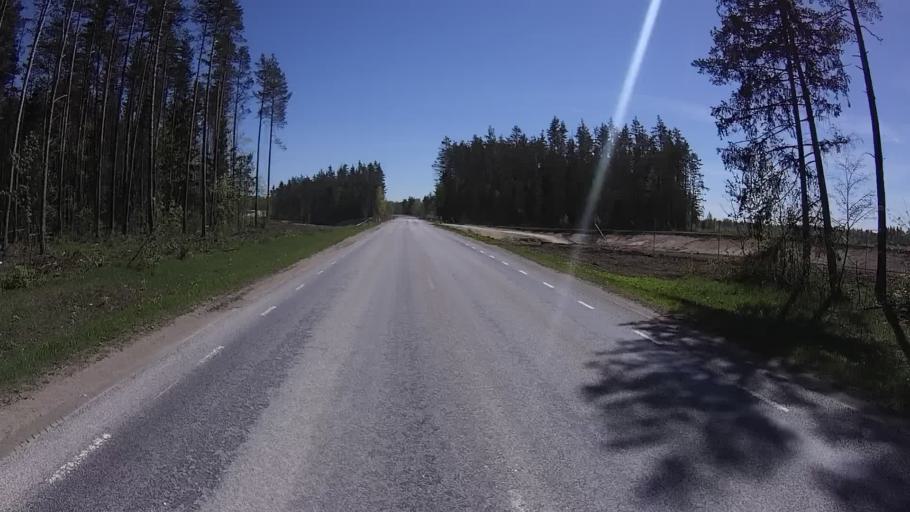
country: EE
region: Harju
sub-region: Raasiku vald
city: Raasiku
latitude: 59.1615
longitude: 25.1813
